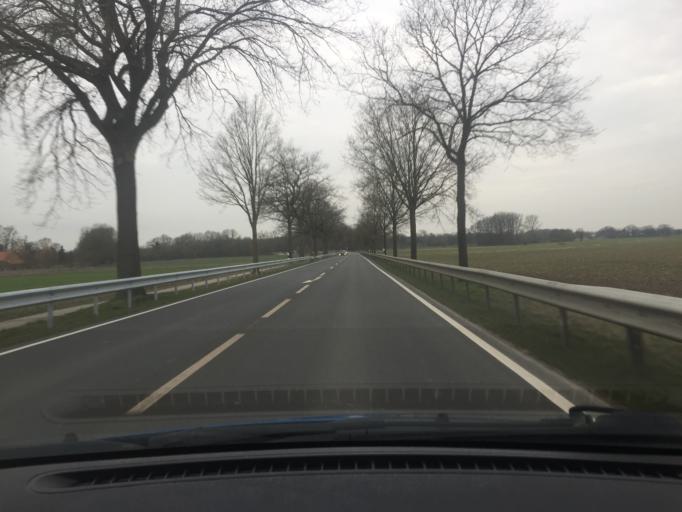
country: DE
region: Lower Saxony
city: Kusten
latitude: 52.9810
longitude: 11.0996
